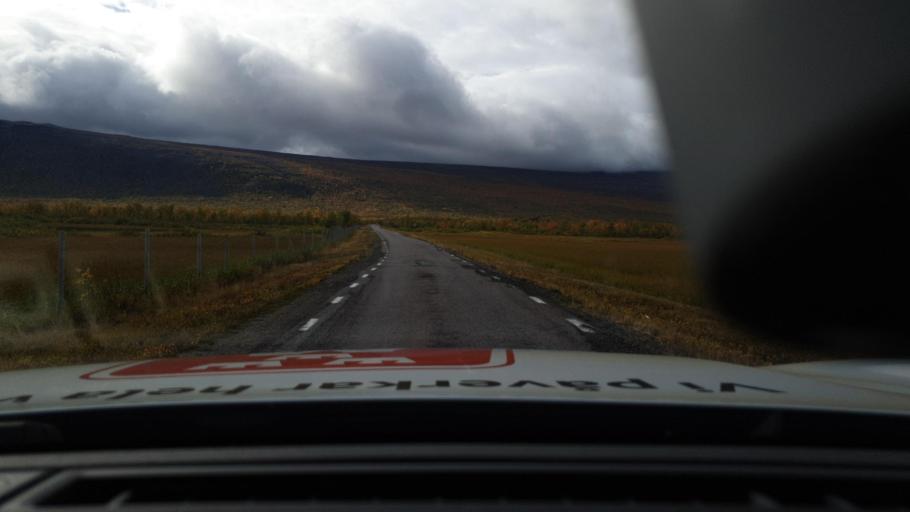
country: SE
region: Norrbotten
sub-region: Kiruna Kommun
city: Kiruna
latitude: 67.8595
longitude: 19.0265
